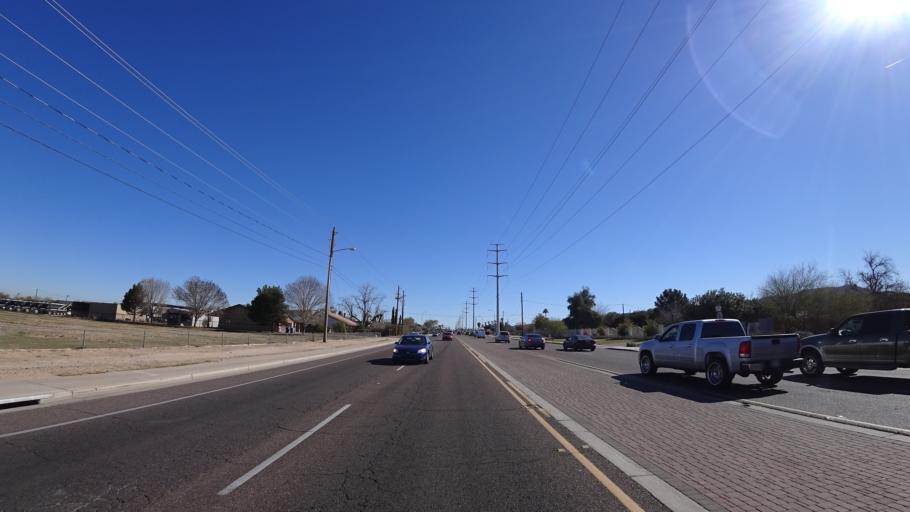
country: US
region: Arizona
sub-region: Maricopa County
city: Laveen
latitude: 33.3778
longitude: -112.1047
